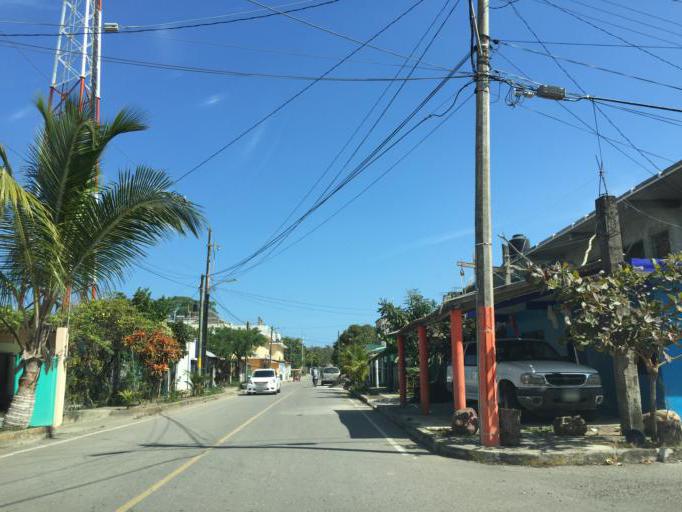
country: MX
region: Veracruz
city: Tecolutla
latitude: 20.4789
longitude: -97.0141
